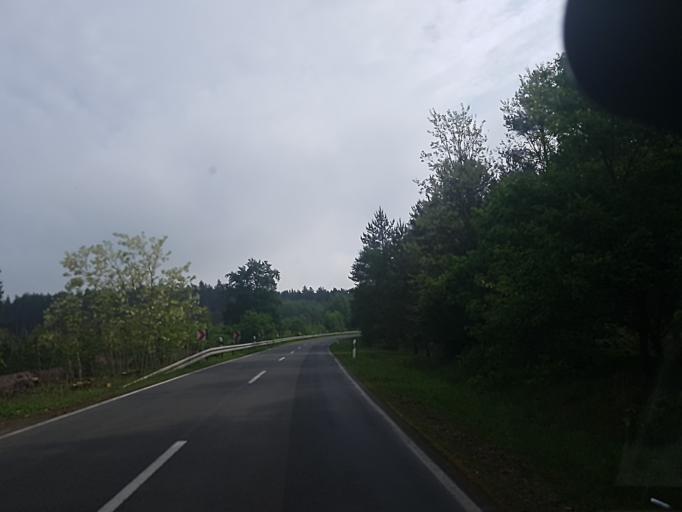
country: DE
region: Brandenburg
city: Gorzke
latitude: 52.0944
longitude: 12.3363
